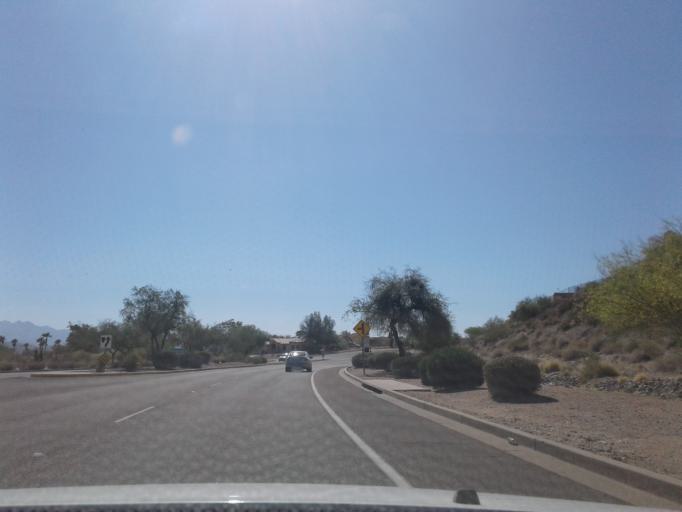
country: US
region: Arizona
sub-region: Maricopa County
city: Fountain Hills
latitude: 33.6141
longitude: -111.7340
